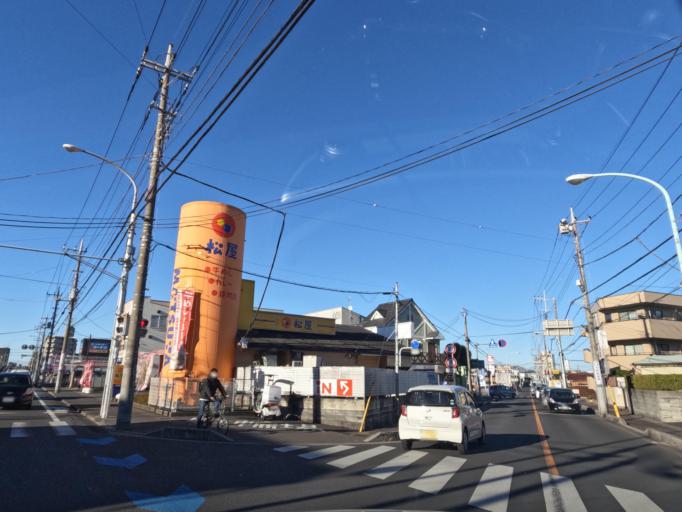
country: JP
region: Saitama
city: Hasuda
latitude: 35.9432
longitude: 139.6425
